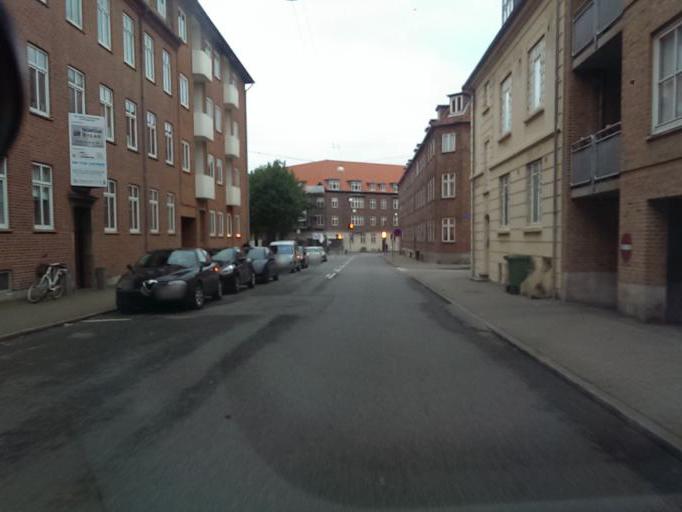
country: DK
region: South Denmark
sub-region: Esbjerg Kommune
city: Esbjerg
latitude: 55.4707
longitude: 8.4405
